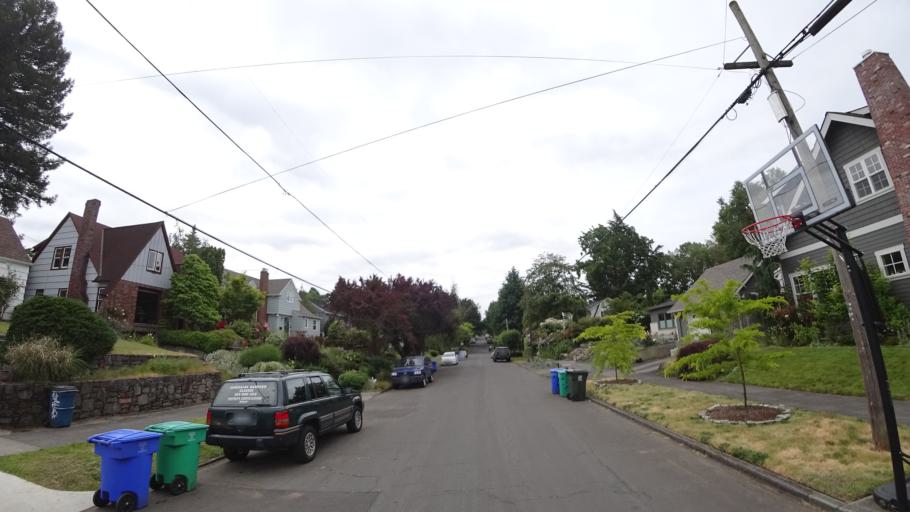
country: US
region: Oregon
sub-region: Multnomah County
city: Portland
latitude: 45.5239
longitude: -122.6173
